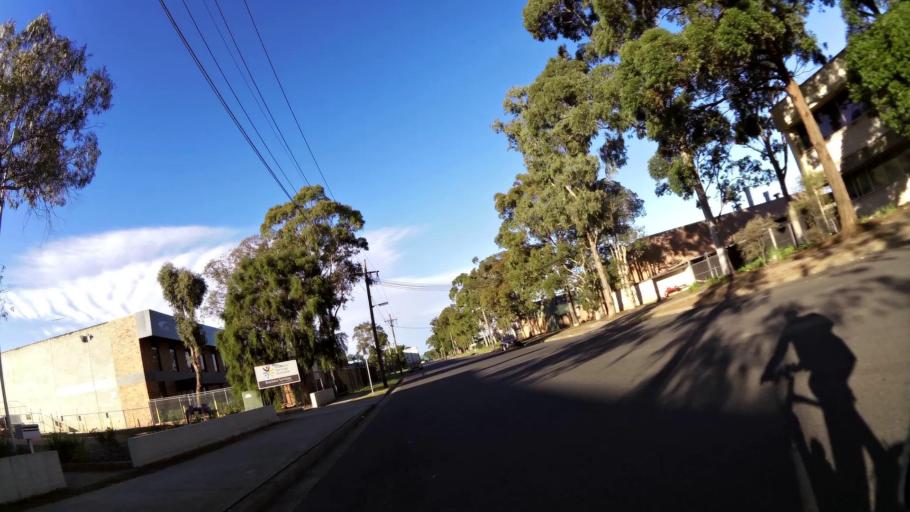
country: AU
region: New South Wales
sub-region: Bankstown
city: Milperra
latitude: -33.9204
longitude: 150.9985
